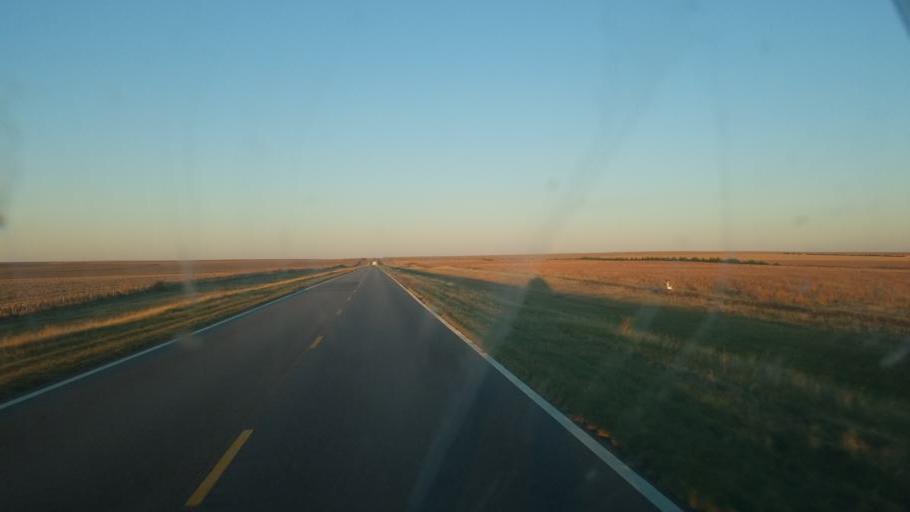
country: US
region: Kansas
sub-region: Wallace County
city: Sharon Springs
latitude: 38.9011
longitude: -101.7988
